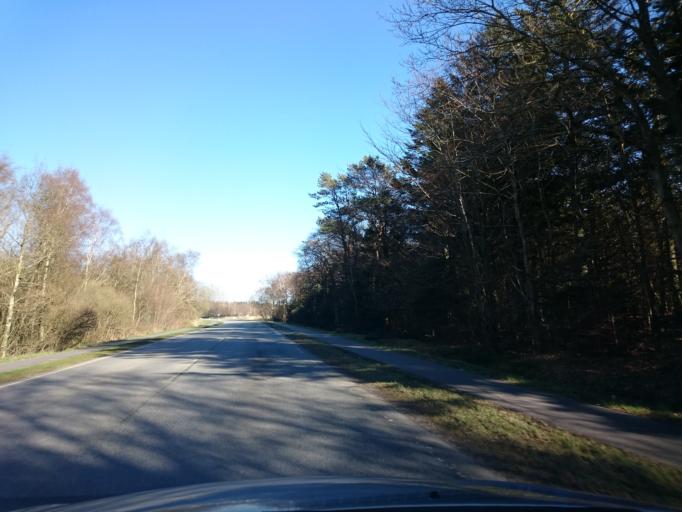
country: DK
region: North Denmark
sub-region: Hjorring Kommune
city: Sindal
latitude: 57.5809
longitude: 10.2066
